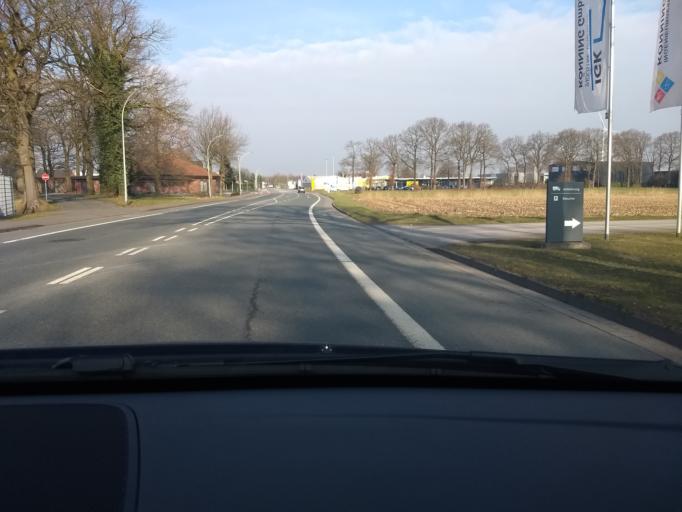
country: DE
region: North Rhine-Westphalia
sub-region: Regierungsbezirk Munster
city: Borken
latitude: 51.8539
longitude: 6.8815
